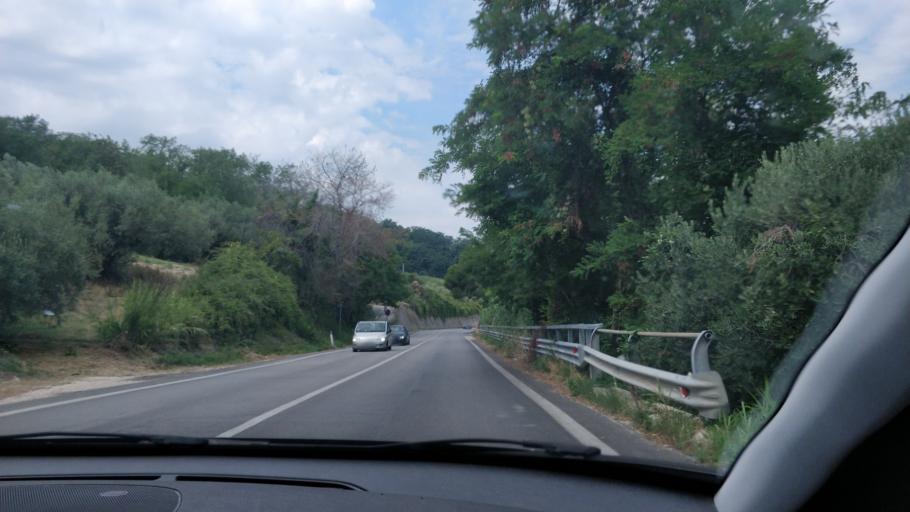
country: IT
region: Abruzzo
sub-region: Provincia di Chieti
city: Marina di San Vito
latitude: 42.3196
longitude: 14.4315
